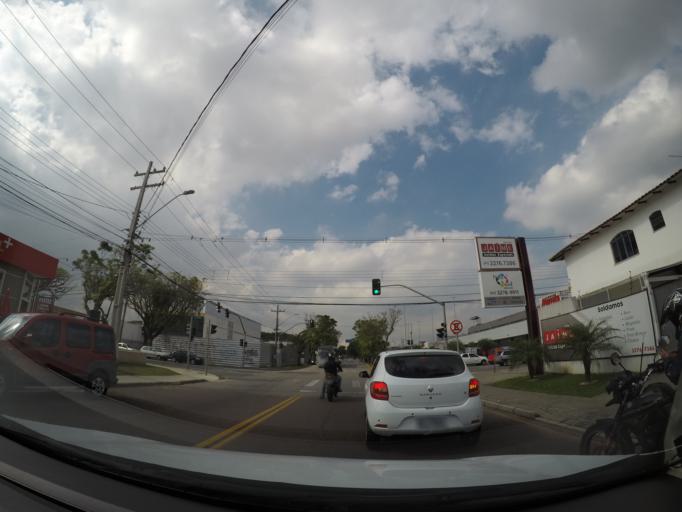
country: BR
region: Parana
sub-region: Curitiba
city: Curitiba
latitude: -25.4834
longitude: -49.2480
